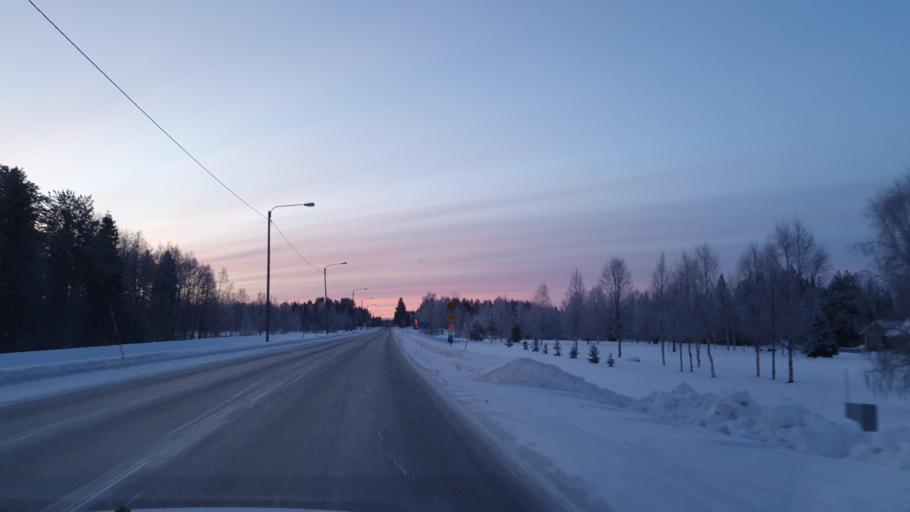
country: FI
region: Lapland
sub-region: Tunturi-Lappi
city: Kolari
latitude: 67.1317
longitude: 23.9820
